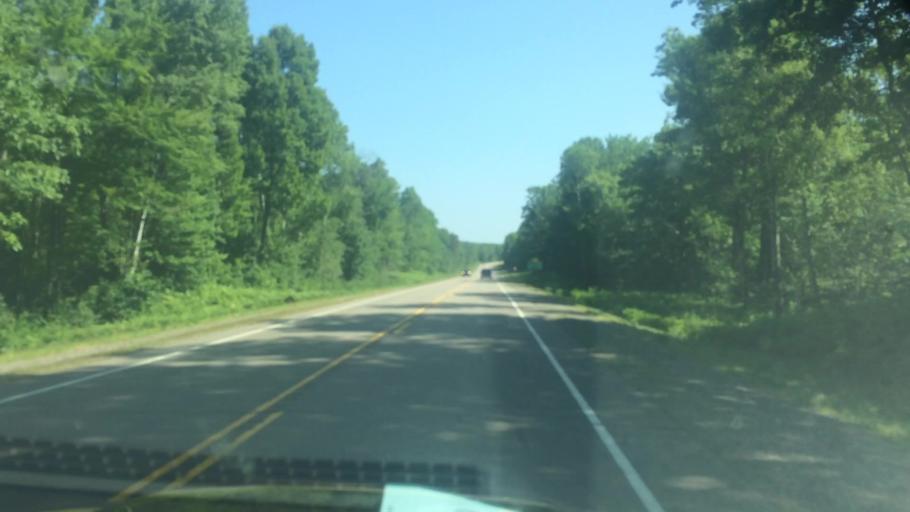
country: US
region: Wisconsin
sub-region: Lincoln County
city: Tomahawk
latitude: 45.5603
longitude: -89.6477
